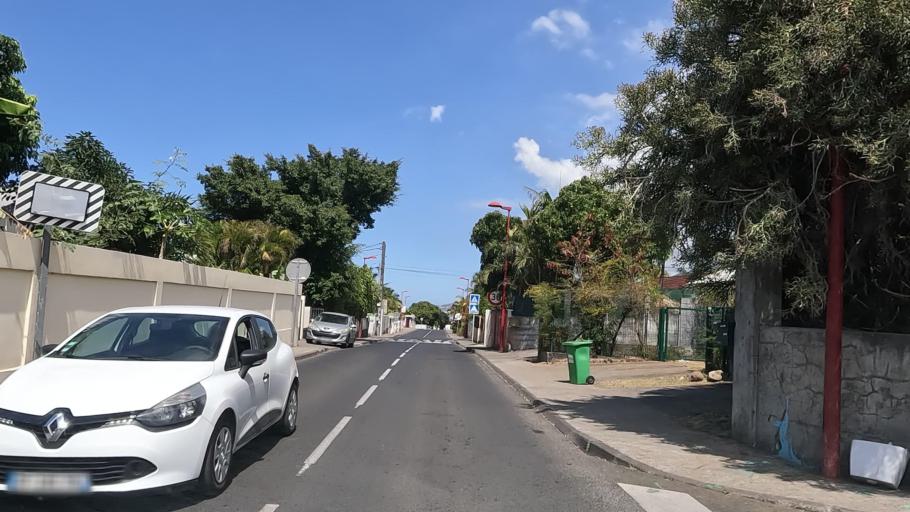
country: RE
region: Reunion
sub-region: Reunion
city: Saint-Louis
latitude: -21.2780
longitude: 55.4480
